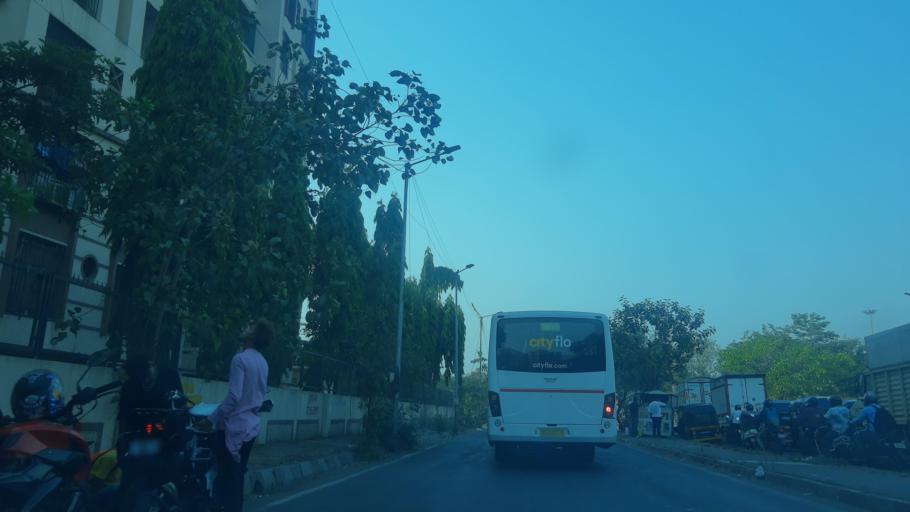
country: IN
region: Maharashtra
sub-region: Thane
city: Thane
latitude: 19.1736
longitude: 72.9682
